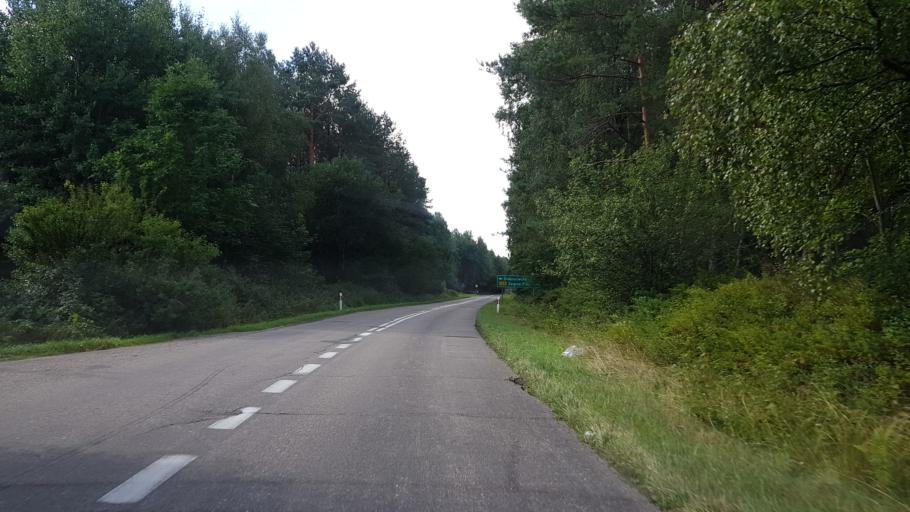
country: PL
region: West Pomeranian Voivodeship
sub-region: Powiat bialogardzki
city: Tychowo
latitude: 54.0509
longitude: 16.3001
